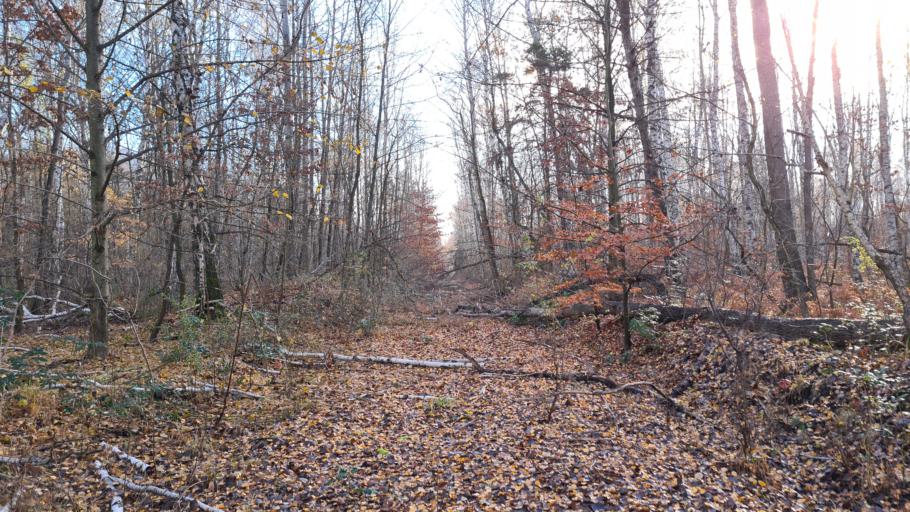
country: DE
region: Brandenburg
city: Sallgast
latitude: 51.5685
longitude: 13.8678
